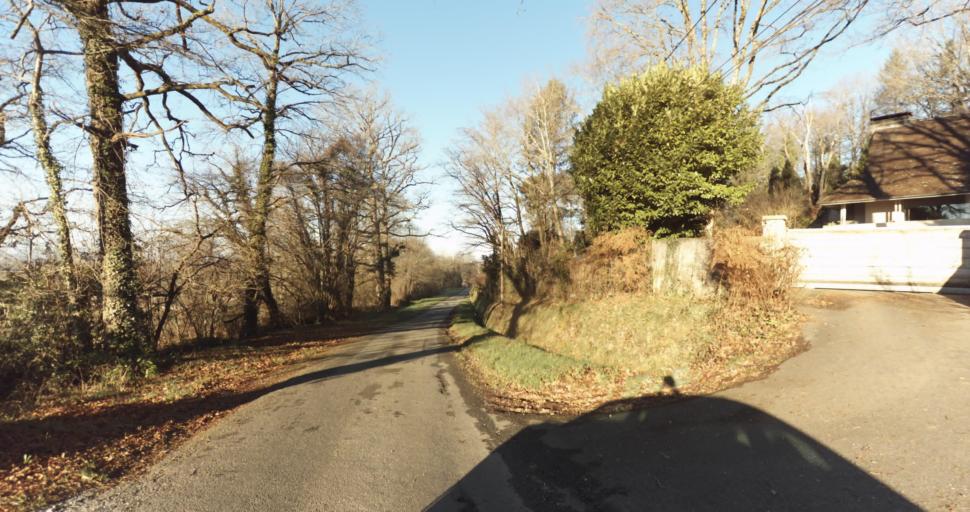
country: FR
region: Aquitaine
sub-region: Departement des Pyrenees-Atlantiques
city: Ousse
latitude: 43.3116
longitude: -0.2426
